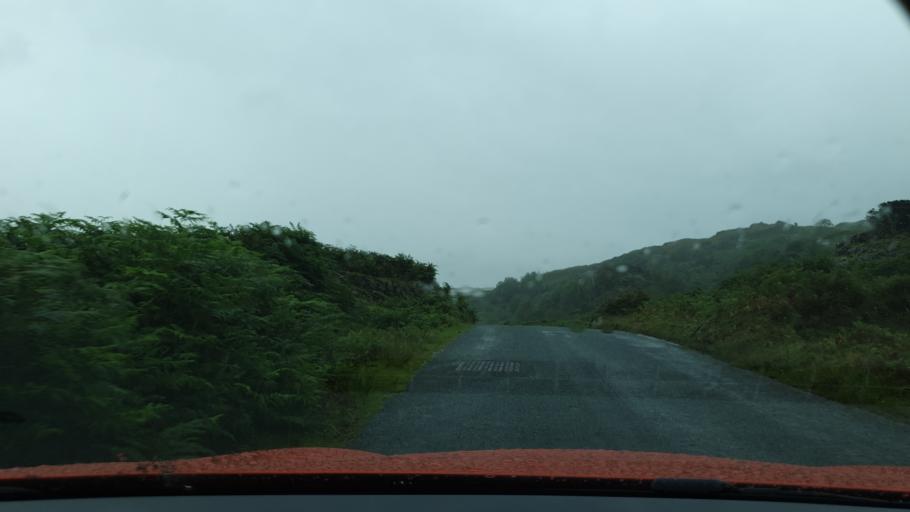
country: GB
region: England
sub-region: Cumbria
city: Millom
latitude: 54.3184
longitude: -3.2338
